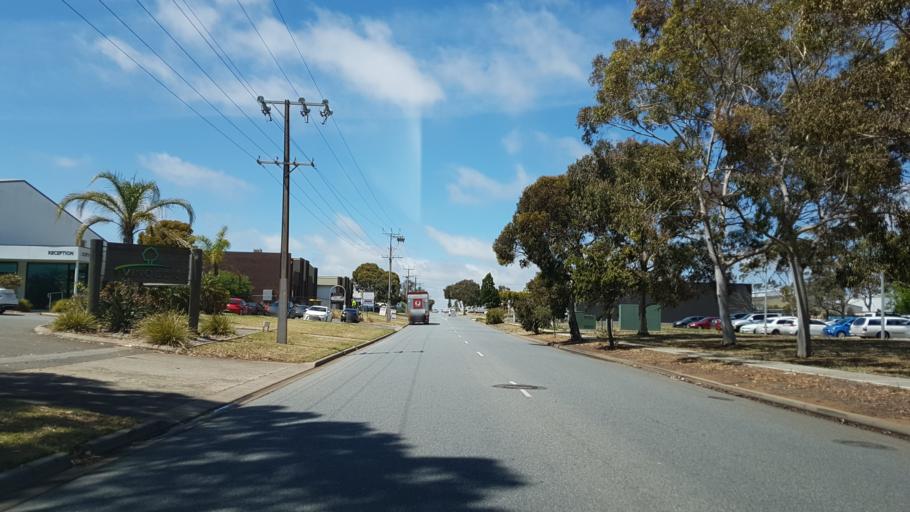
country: AU
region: South Australia
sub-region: Onkaparinga
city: Morphett Vale
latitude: -35.1089
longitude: 138.5071
